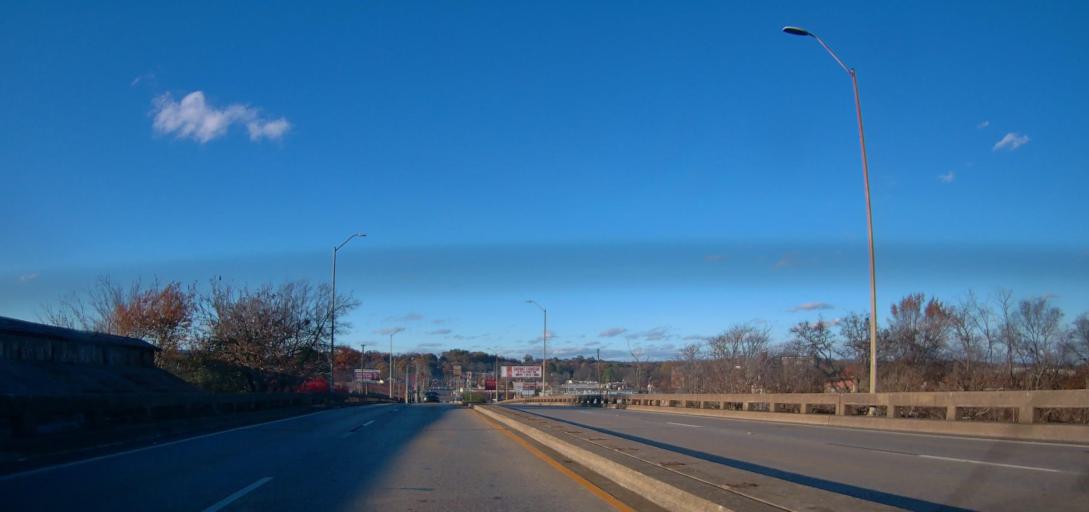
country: US
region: Alabama
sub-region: Jefferson County
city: Birmingham
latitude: 33.5499
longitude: -86.8172
